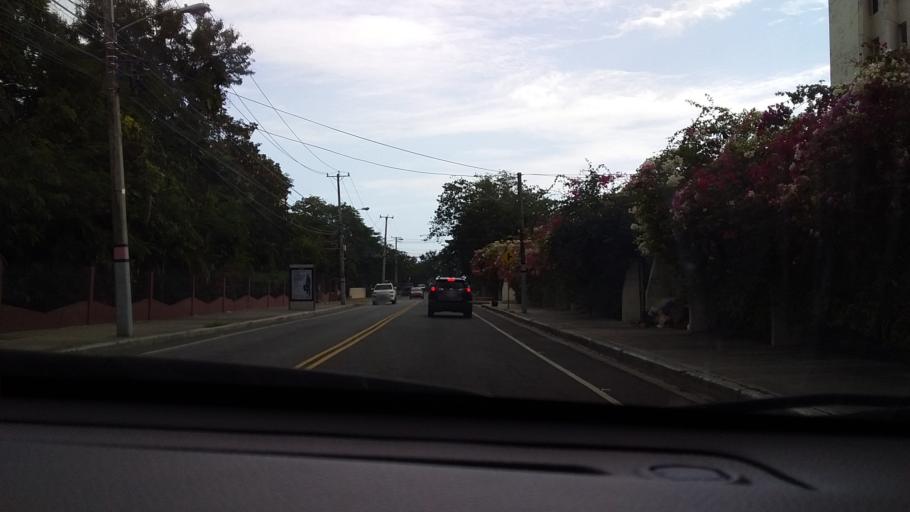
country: DO
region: Nacional
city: Bella Vista
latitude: 18.4538
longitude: -69.9357
